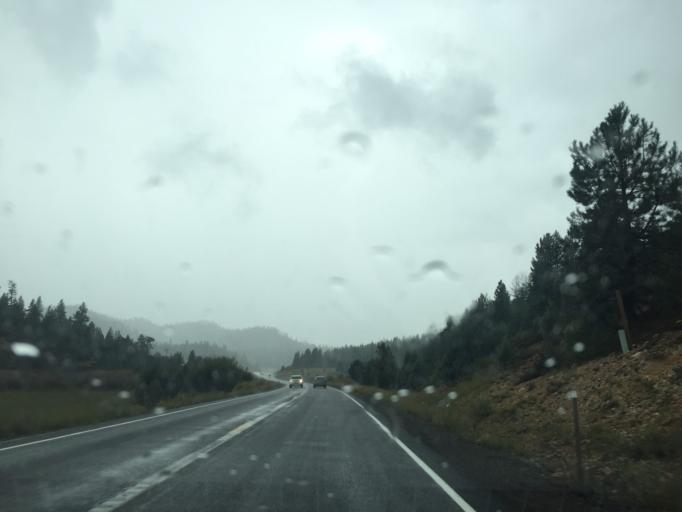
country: US
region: Utah
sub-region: Kane County
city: Kanab
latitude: 37.4339
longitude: -112.5386
